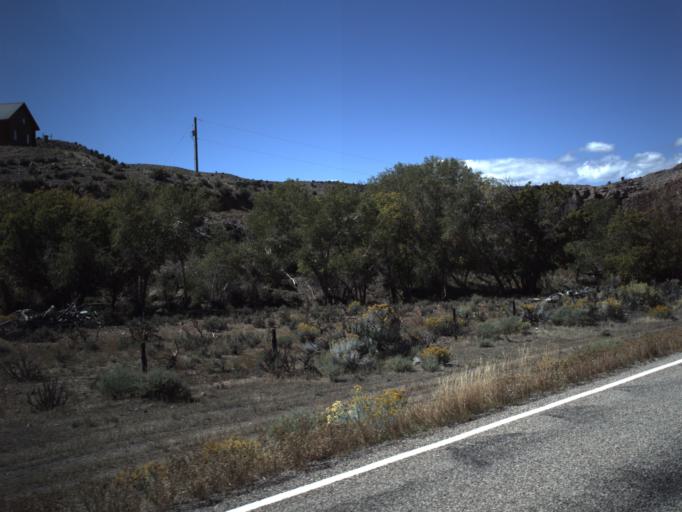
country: US
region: Utah
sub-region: Piute County
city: Junction
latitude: 38.1959
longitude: -112.1464
